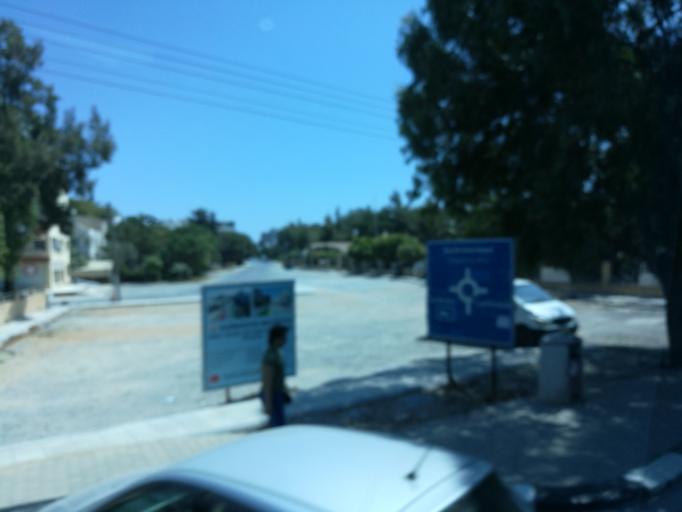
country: CY
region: Ammochostos
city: Famagusta
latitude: 35.1307
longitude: 33.9269
